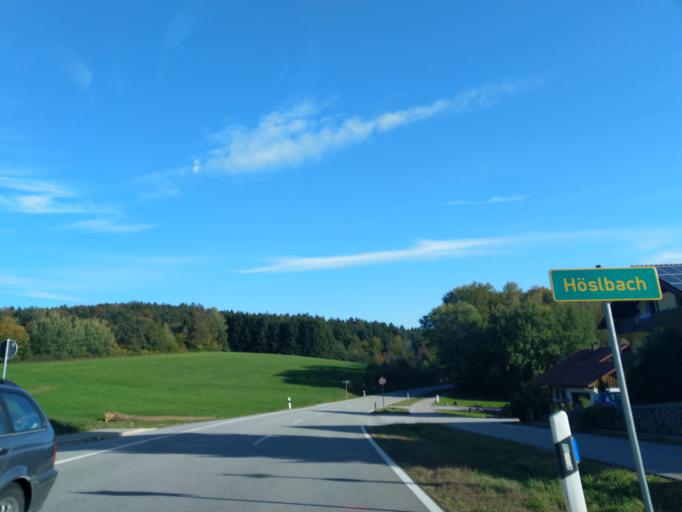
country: DE
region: Bavaria
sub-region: Lower Bavaria
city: Bernried
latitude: 48.9081
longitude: 12.8871
